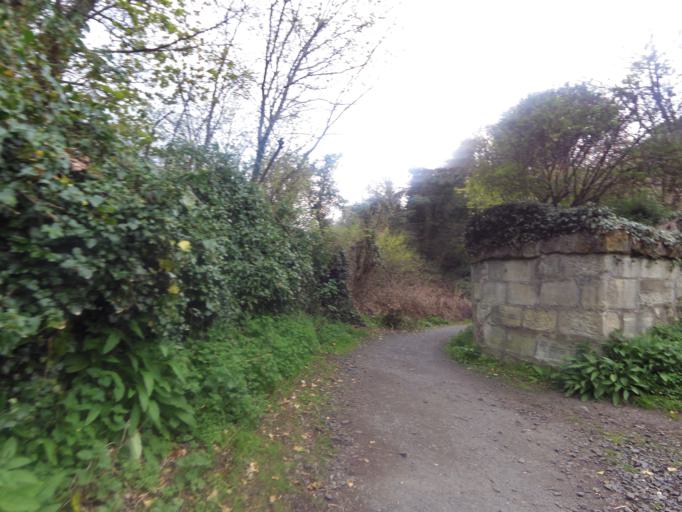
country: GB
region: Scotland
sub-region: Fife
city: Burntisland
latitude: 56.0601
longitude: -3.2615
